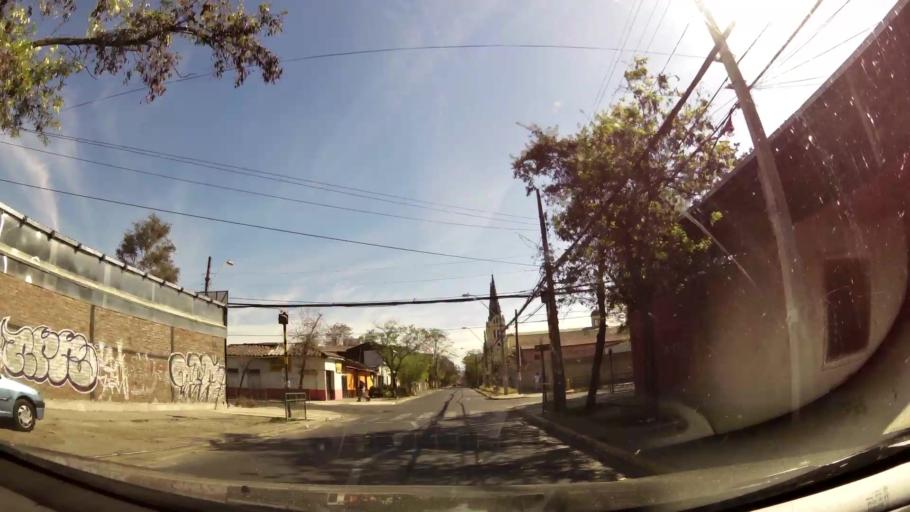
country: CL
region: Santiago Metropolitan
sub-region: Provincia de Santiago
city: Santiago
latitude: -33.4263
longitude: -70.6587
